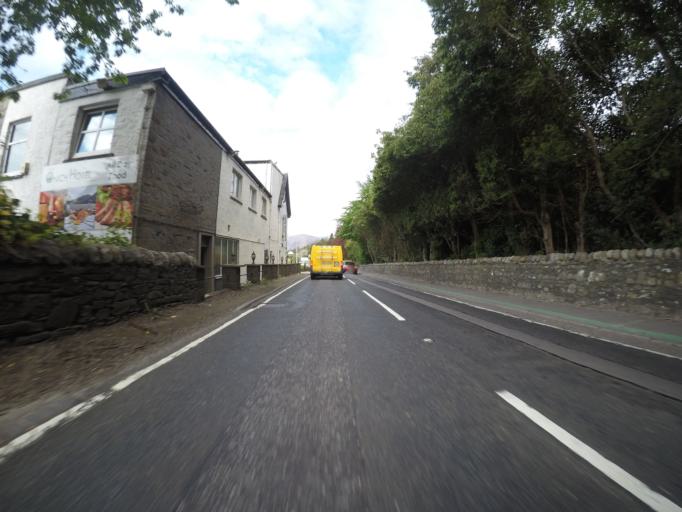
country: GB
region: Scotland
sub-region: Highland
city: Fort William
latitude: 56.7027
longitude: -5.2153
